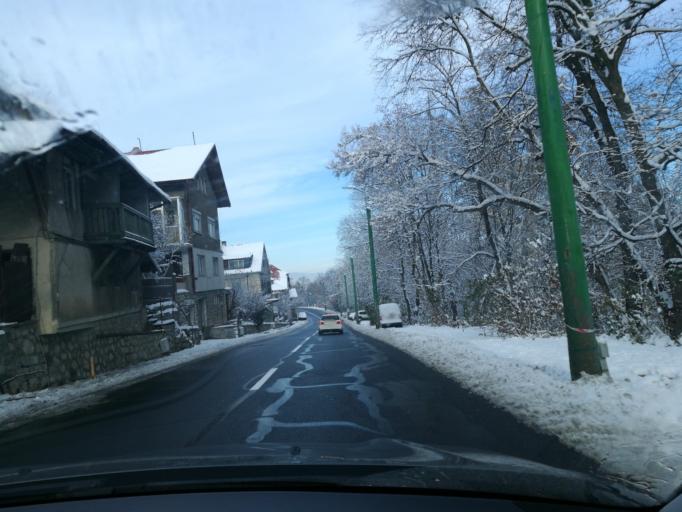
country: RO
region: Brasov
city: Brasov
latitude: 45.6447
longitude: 25.5857
